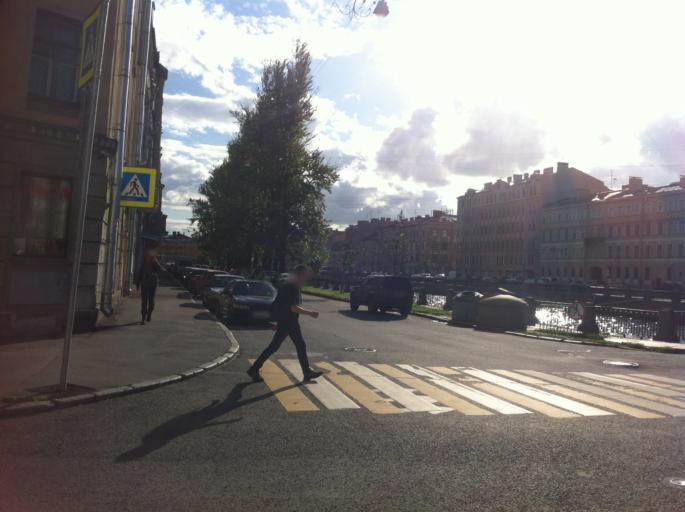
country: RU
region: St.-Petersburg
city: Admiralteisky
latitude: 59.9202
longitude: 30.2874
